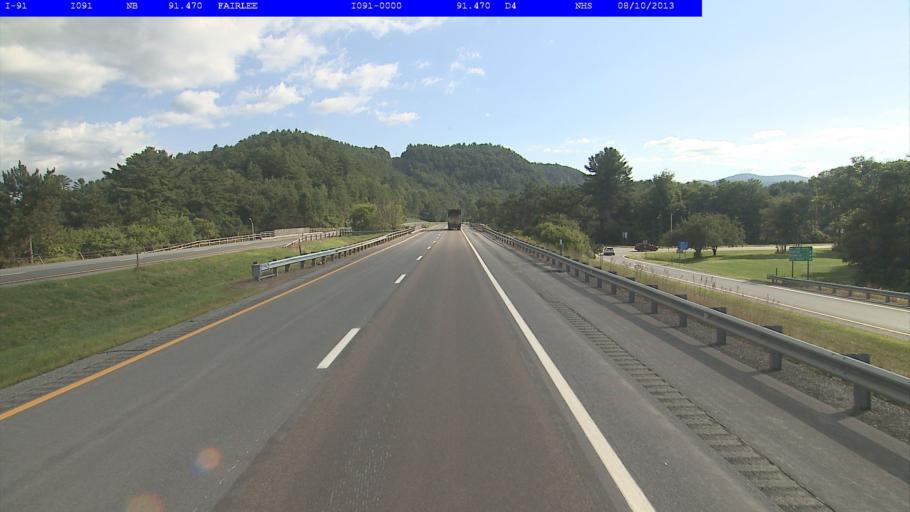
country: US
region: New Hampshire
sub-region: Grafton County
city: Orford
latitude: 43.9045
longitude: -72.1527
